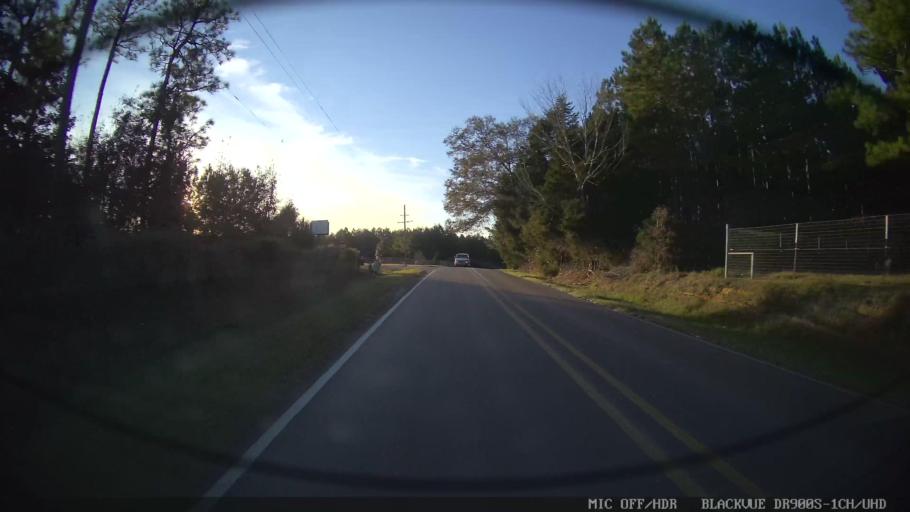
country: US
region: Mississippi
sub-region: Lamar County
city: Lumberton
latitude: 30.9981
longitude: -89.4038
